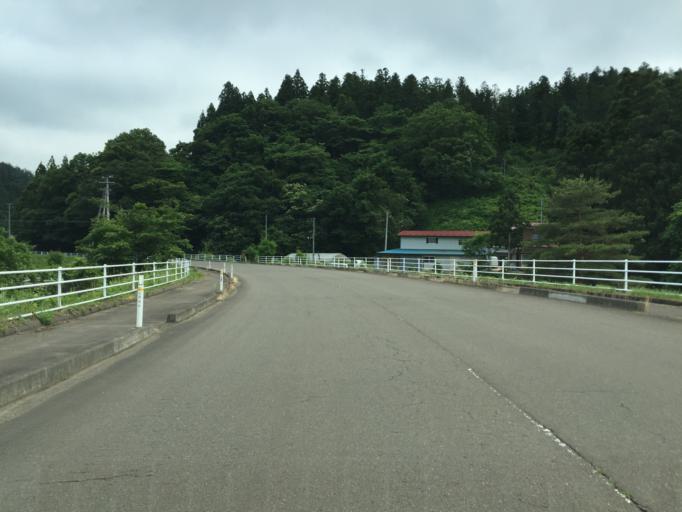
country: JP
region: Miyagi
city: Marumori
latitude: 37.8246
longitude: 140.7275
